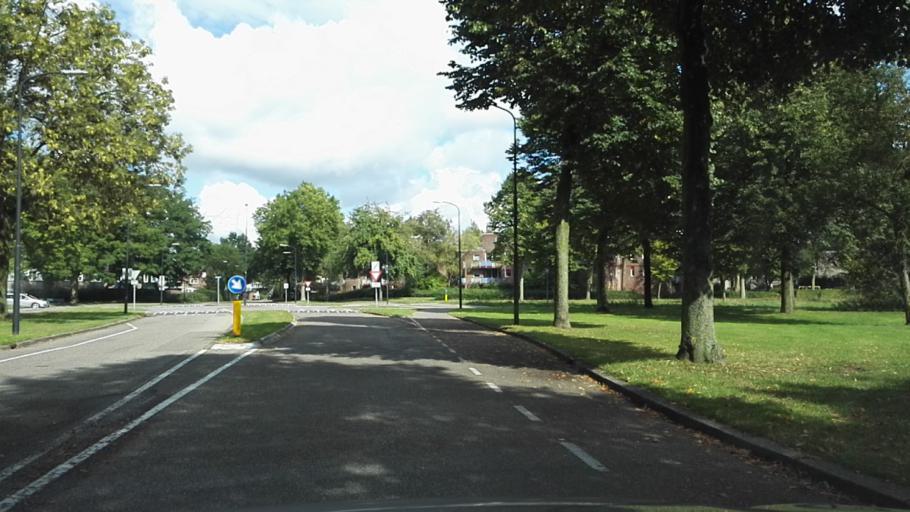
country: NL
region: Gelderland
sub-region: Gemeente Apeldoorn
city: Apeldoorn
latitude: 52.2031
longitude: 5.9882
